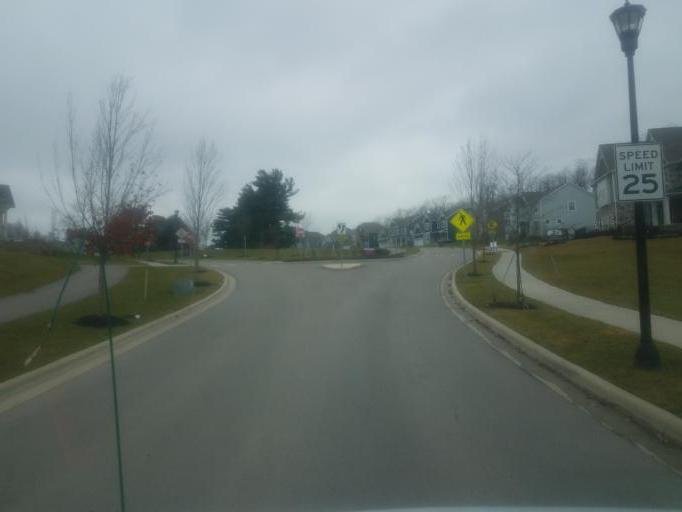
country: US
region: Ohio
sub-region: Franklin County
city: Westerville
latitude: 40.1316
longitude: -82.9516
